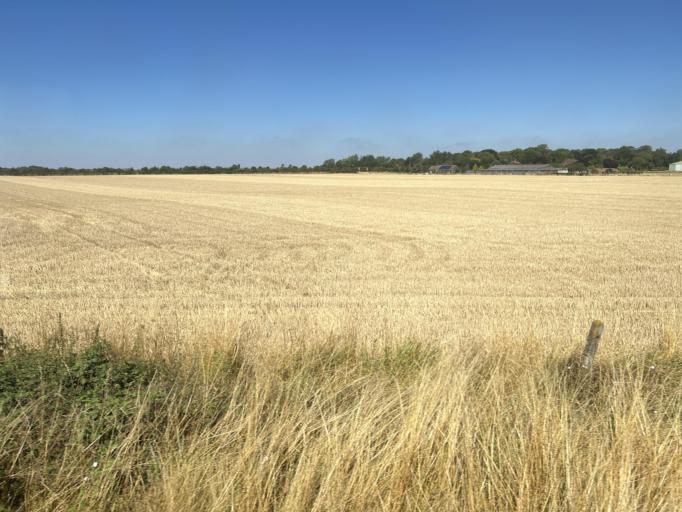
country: GB
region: England
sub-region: Lincolnshire
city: Boston
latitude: 53.0291
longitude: 0.0188
